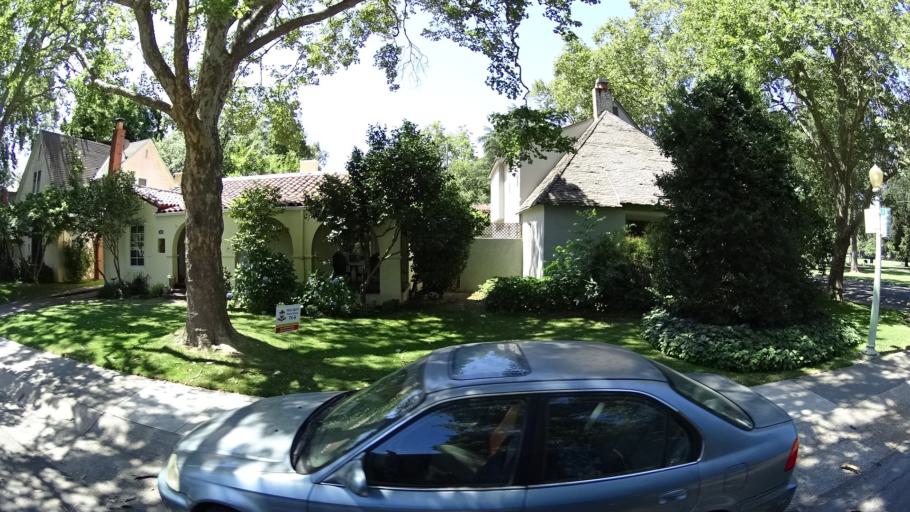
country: US
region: California
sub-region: Sacramento County
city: Sacramento
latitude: 38.5457
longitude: -121.5000
